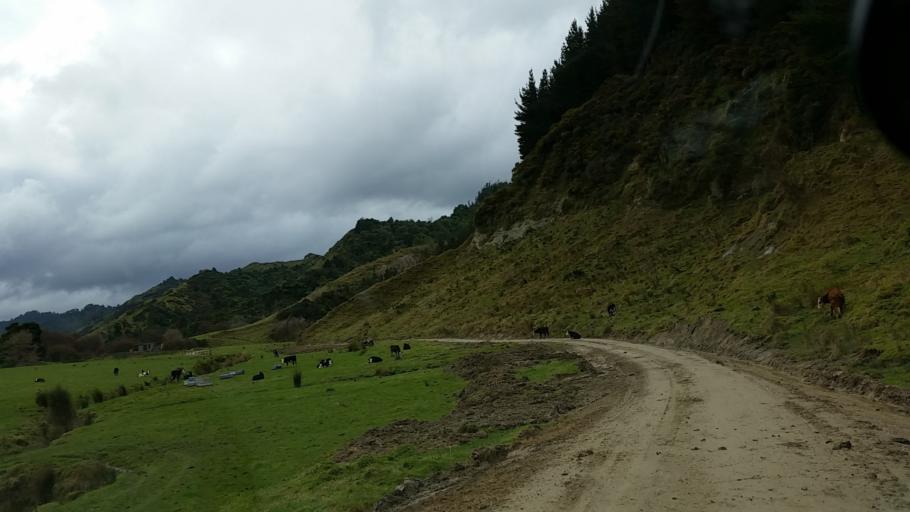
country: NZ
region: Taranaki
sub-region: South Taranaki District
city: Patea
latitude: -39.6627
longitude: 174.7485
